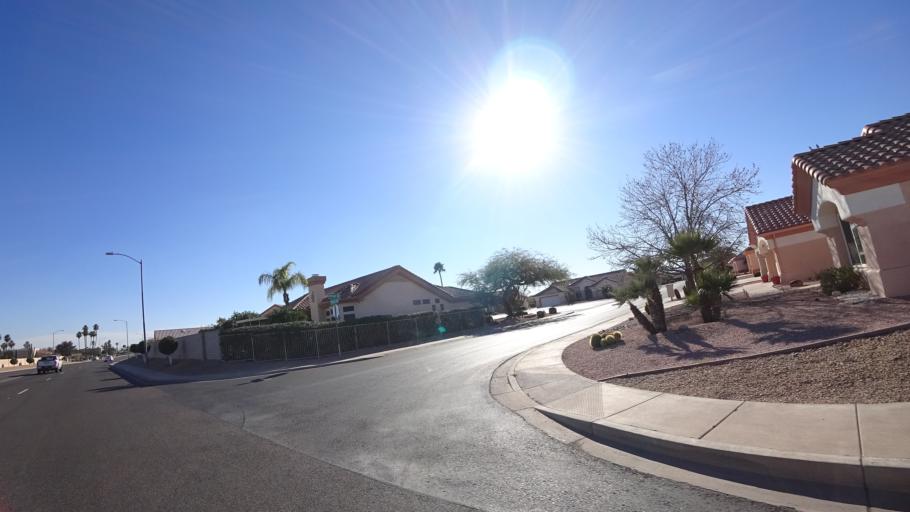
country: US
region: Arizona
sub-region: Maricopa County
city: Sun City West
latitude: 33.6684
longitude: -112.3325
